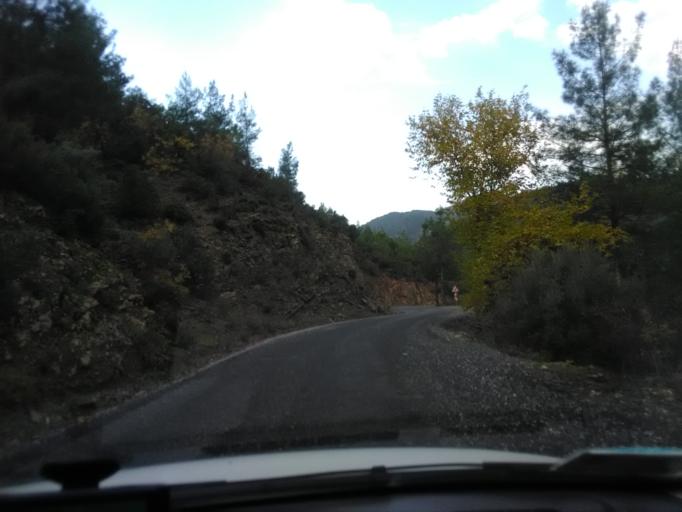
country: TR
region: Antalya
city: Gazipasa
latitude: 36.3033
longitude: 32.3943
